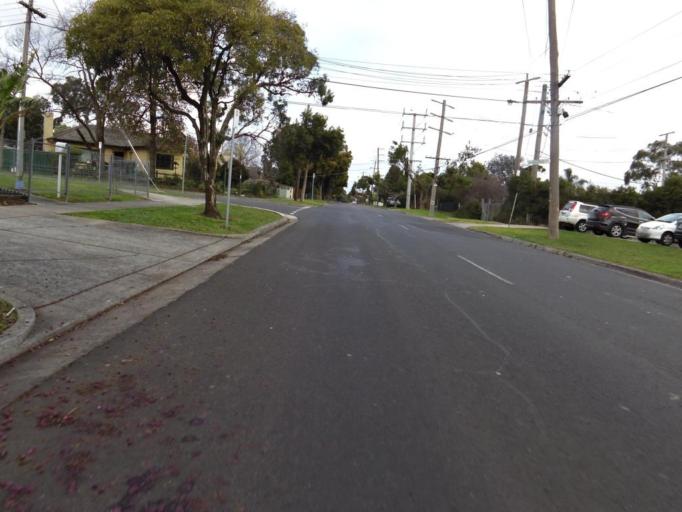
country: AU
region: Victoria
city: Mitcham
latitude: -37.8218
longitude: 145.2205
